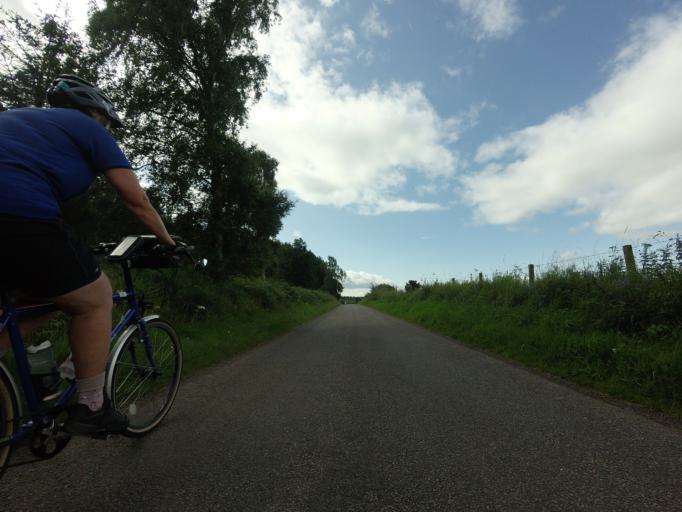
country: GB
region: Scotland
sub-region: Highland
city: Nairn
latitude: 57.5664
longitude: -3.8666
